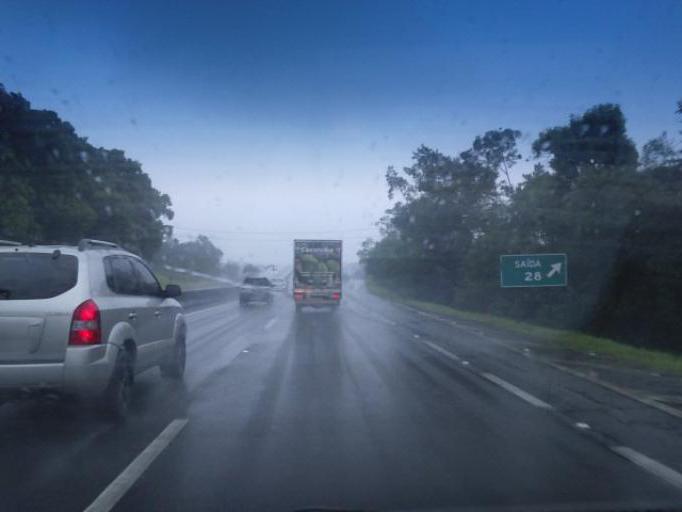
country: BR
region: Santa Catarina
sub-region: Joinville
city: Joinville
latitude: -26.2060
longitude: -48.9144
